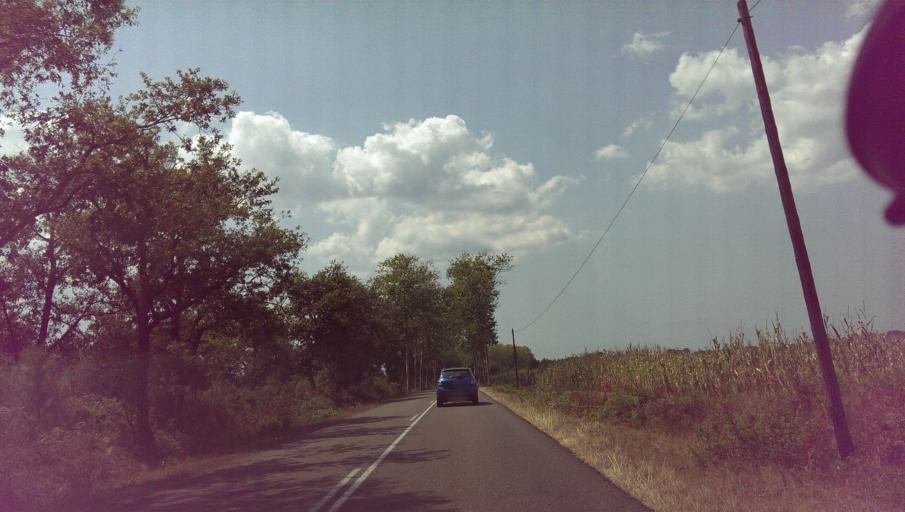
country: FR
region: Aquitaine
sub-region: Departement des Landes
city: Sabres
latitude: 44.1193
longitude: -0.6475
